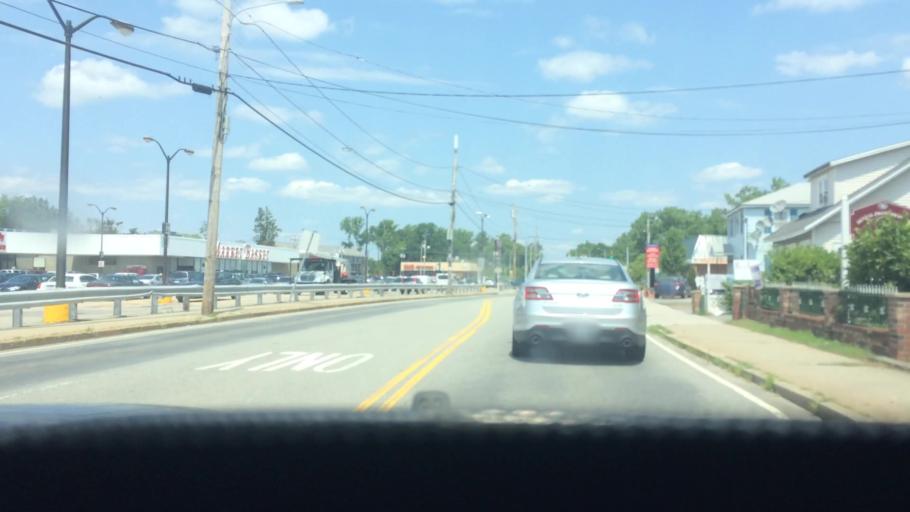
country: US
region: Massachusetts
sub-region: Middlesex County
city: Chelmsford
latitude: 42.6331
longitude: -71.3554
